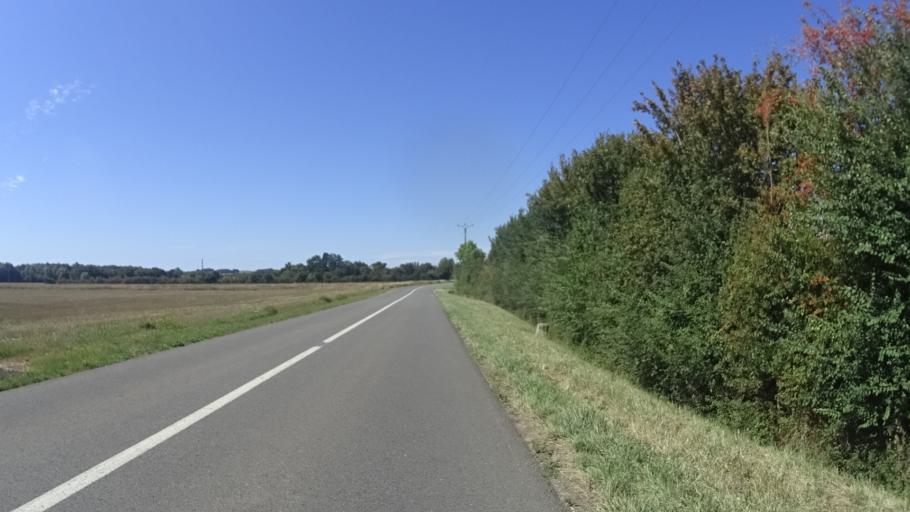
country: FR
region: Centre
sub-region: Departement du Cher
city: Belleville-sur-Loire
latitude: 47.5104
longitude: 2.8651
